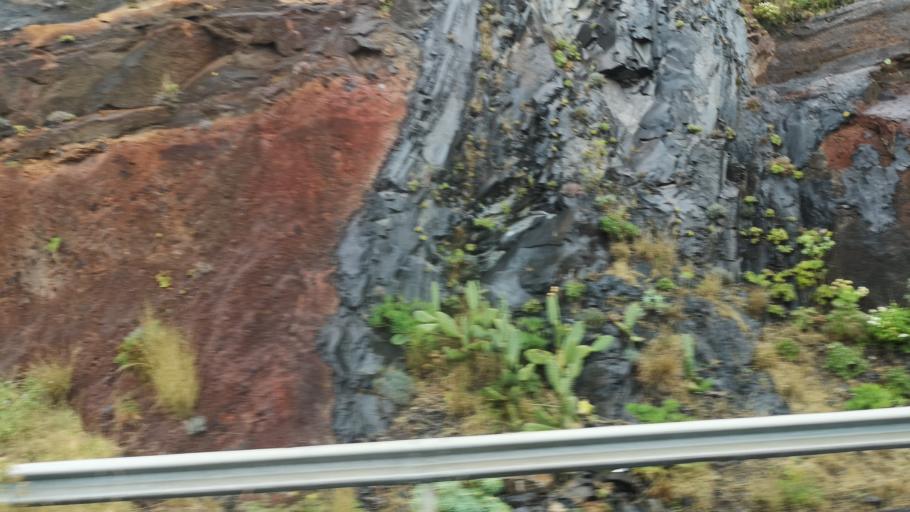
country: ES
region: Canary Islands
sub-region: Provincia de Santa Cruz de Tenerife
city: Alajero
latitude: 28.0944
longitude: -17.1987
